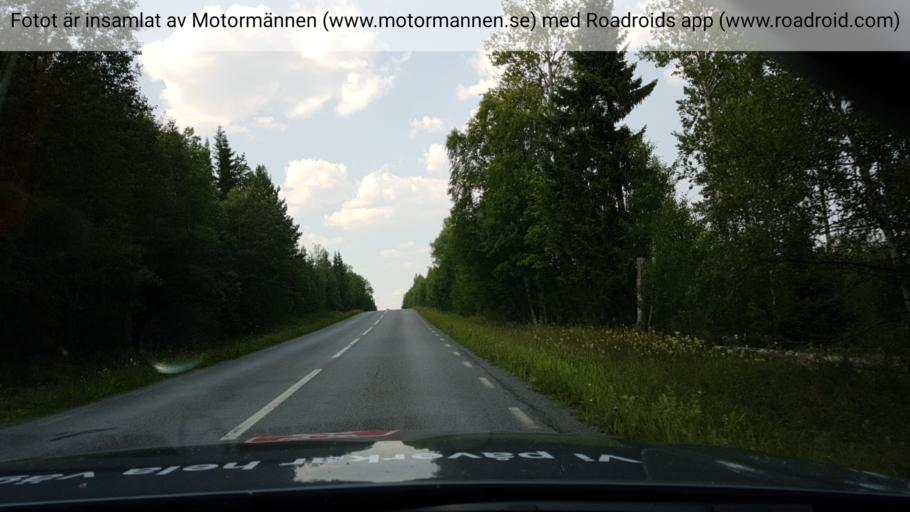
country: SE
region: Jaemtland
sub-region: Krokoms Kommun
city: Krokom
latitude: 63.1579
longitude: 14.1393
